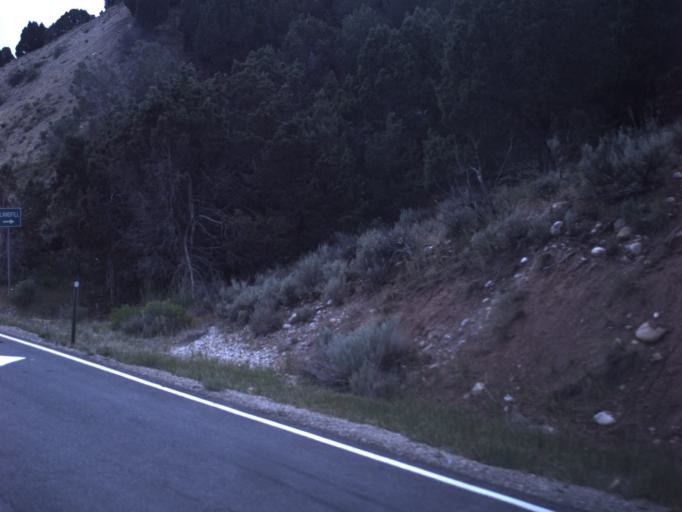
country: US
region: Utah
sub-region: Summit County
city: Oakley
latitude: 40.7622
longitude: -111.3956
